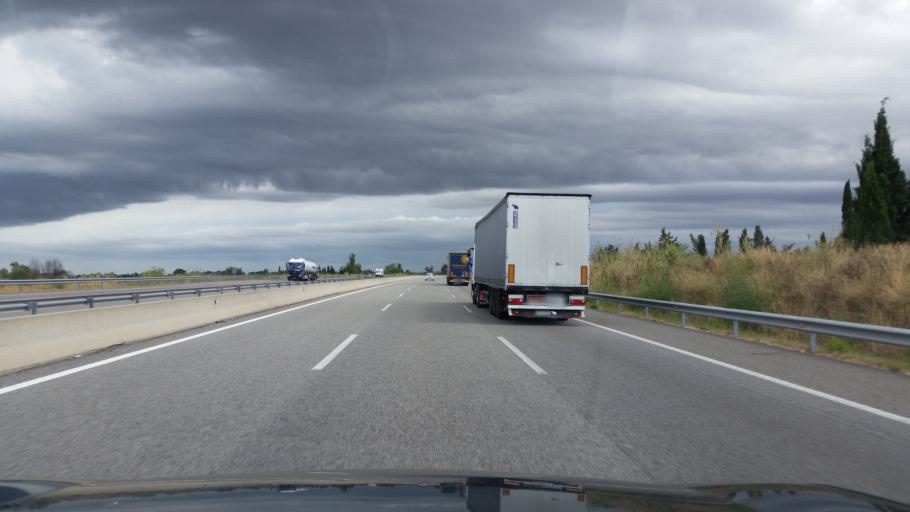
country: ES
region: Catalonia
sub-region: Provincia de Girona
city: Pont de Molins
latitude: 42.3220
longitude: 2.9405
